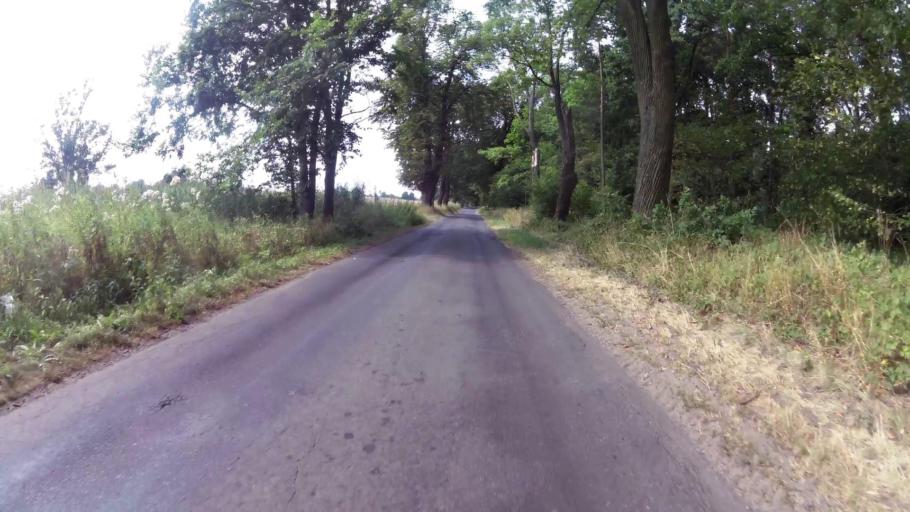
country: PL
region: West Pomeranian Voivodeship
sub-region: Powiat gryfinski
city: Mieszkowice
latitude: 52.8725
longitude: 14.5113
